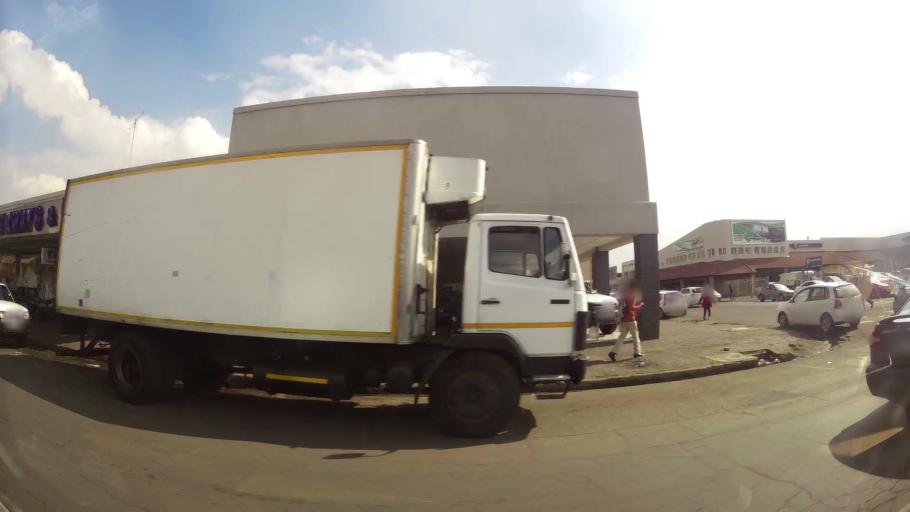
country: ZA
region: Gauteng
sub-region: Sedibeng District Municipality
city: Vereeniging
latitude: -26.6698
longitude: 27.9327
